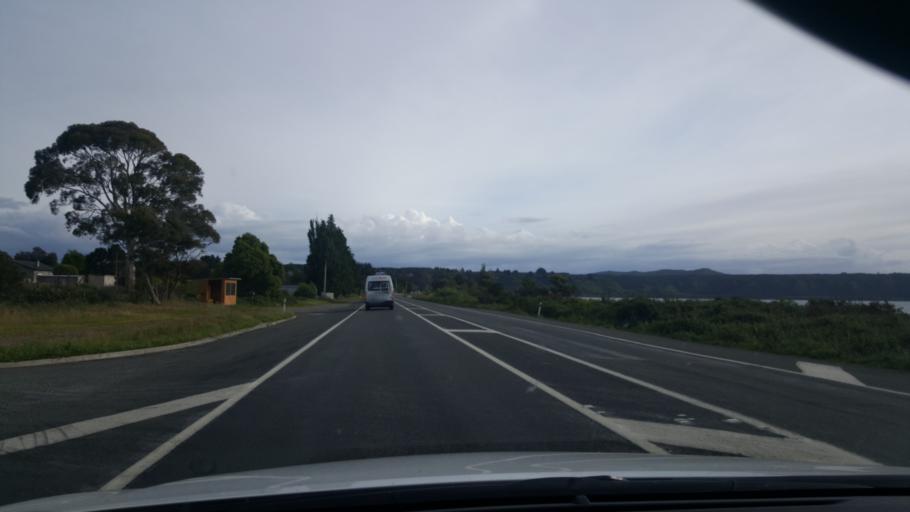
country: NZ
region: Waikato
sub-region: Taupo District
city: Taupo
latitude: -38.7827
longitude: 176.0769
